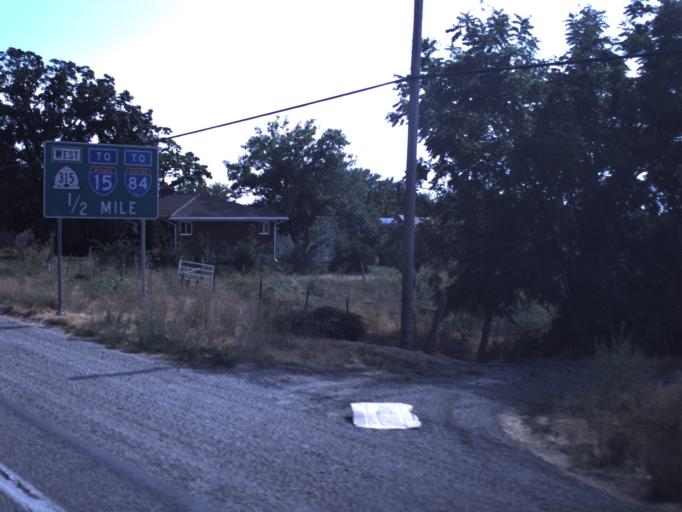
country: US
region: Utah
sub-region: Box Elder County
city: Willard
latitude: 41.4298
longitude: -112.0356
